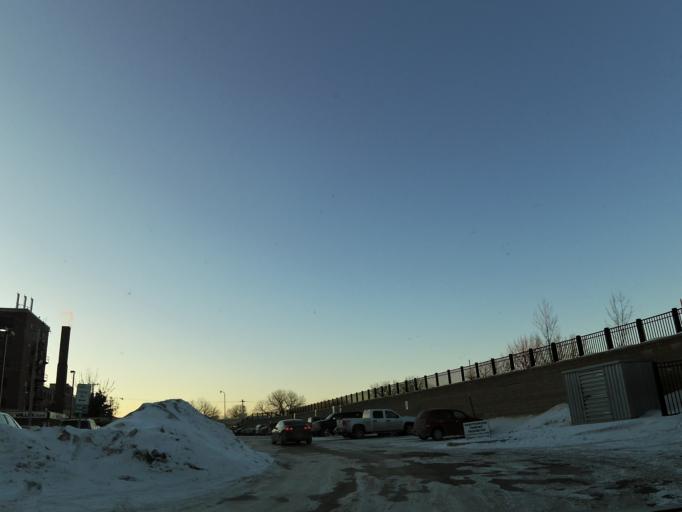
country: US
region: North Dakota
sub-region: Grand Forks County
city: Grand Forks
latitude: 47.9261
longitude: -97.0304
